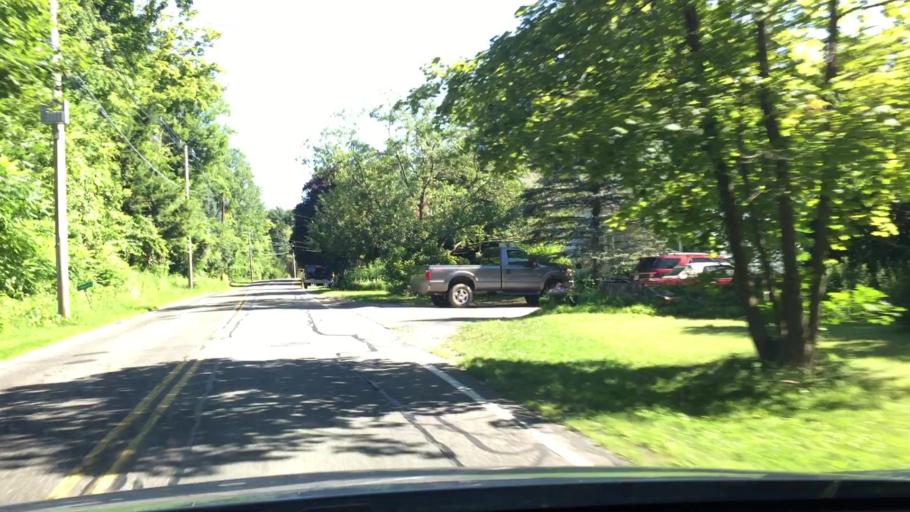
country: US
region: Massachusetts
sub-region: Berkshire County
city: West Stockbridge
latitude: 42.3381
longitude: -73.3673
